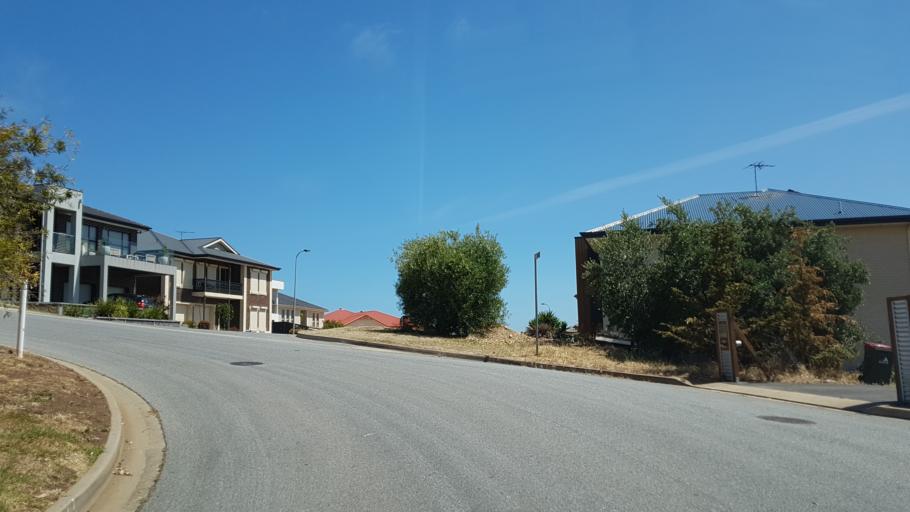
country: AU
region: South Australia
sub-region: Marion
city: Marino
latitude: -35.0632
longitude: 138.5097
